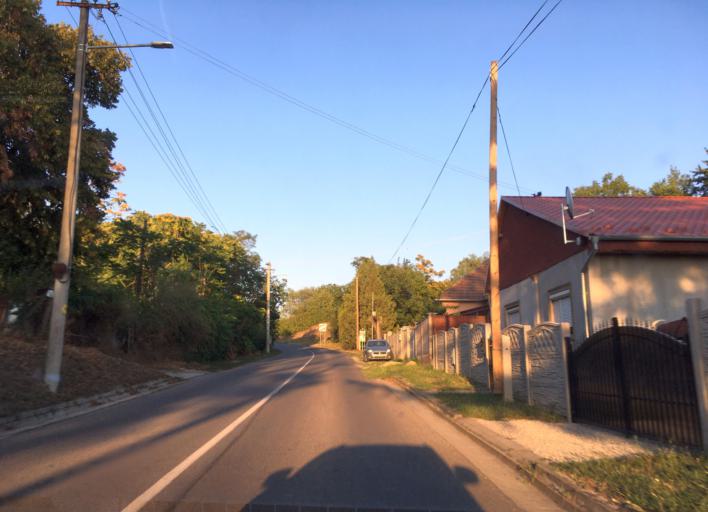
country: HU
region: Komarom-Esztergom
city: Neszmely
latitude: 47.8202
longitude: 18.3591
